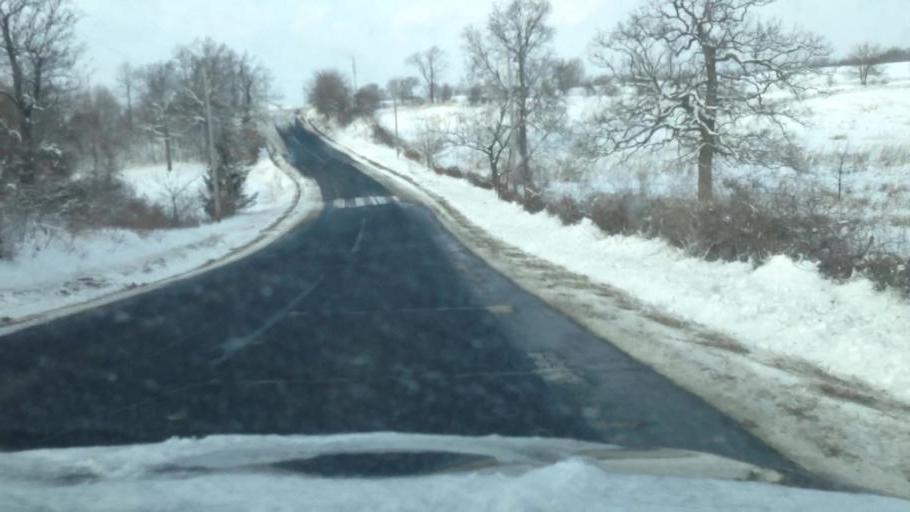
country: US
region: Wisconsin
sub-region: Walworth County
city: East Troy
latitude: 42.7546
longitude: -88.4454
